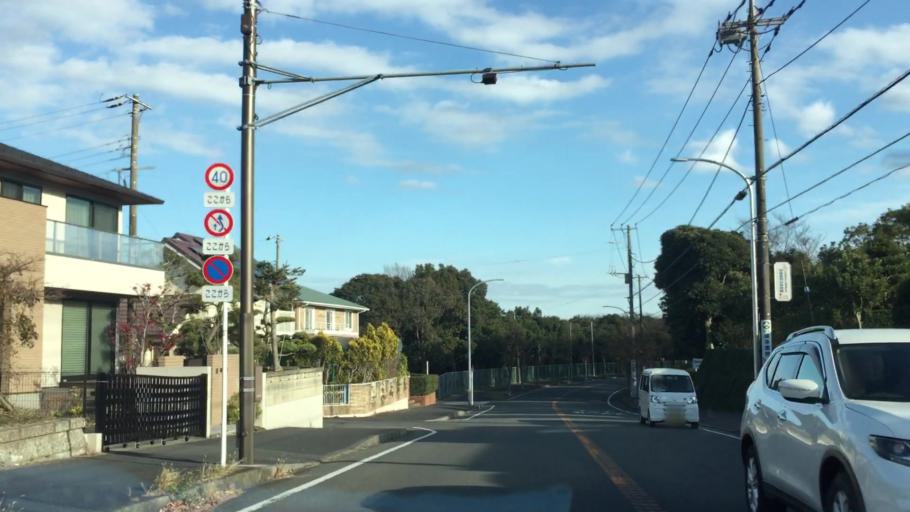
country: JP
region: Kanagawa
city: Zushi
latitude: 35.3394
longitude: 139.5959
